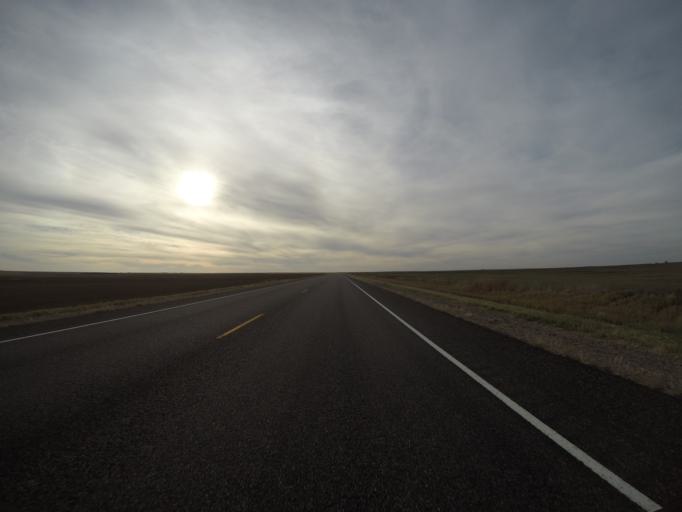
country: US
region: Kansas
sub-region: Cheyenne County
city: Saint Francis
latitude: 39.7465
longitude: -102.0954
